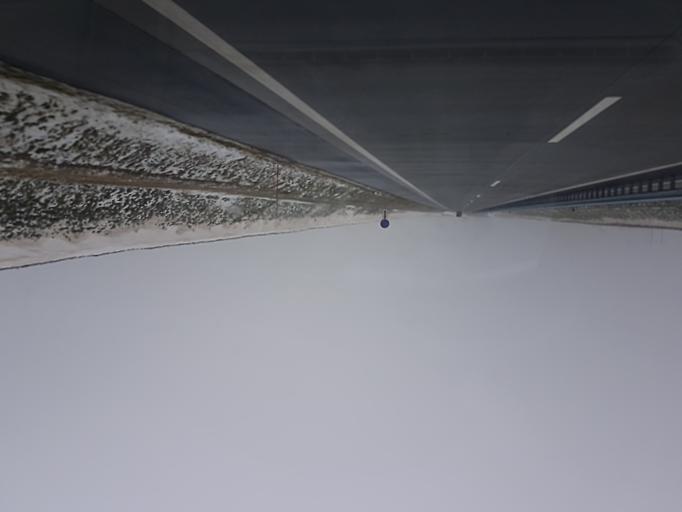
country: BY
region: Minsk
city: Atolina
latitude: 53.7416
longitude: 27.4168
